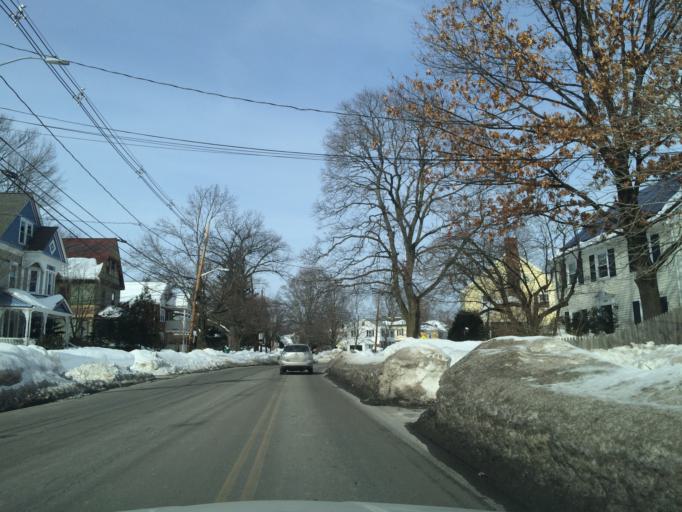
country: US
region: Massachusetts
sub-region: Middlesex County
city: Waltham
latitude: 42.3489
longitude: -71.2473
